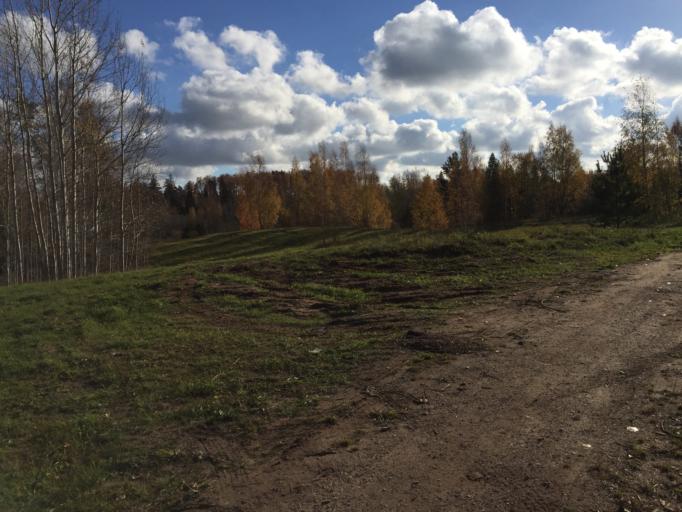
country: LV
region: Tukuma Rajons
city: Tukums
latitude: 56.9628
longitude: 22.9912
